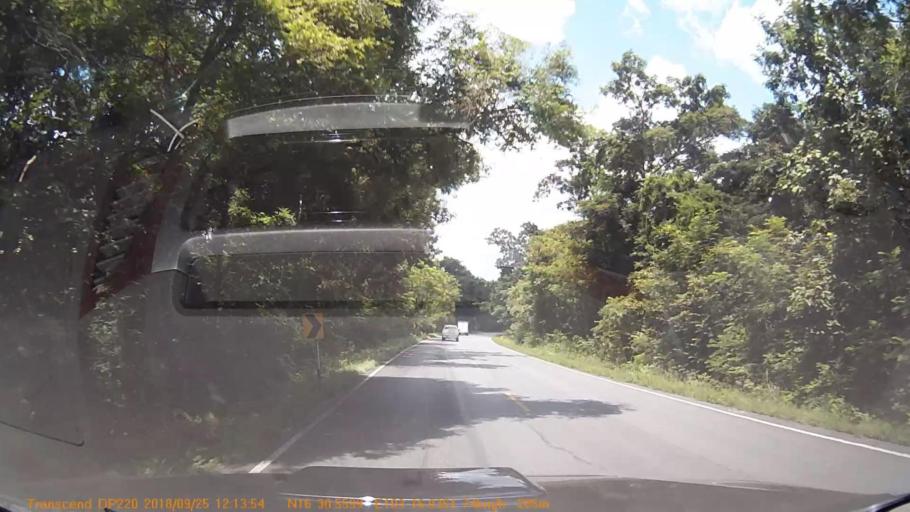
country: TH
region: Kalasin
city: Huai Mek
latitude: 16.5094
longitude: 103.2672
